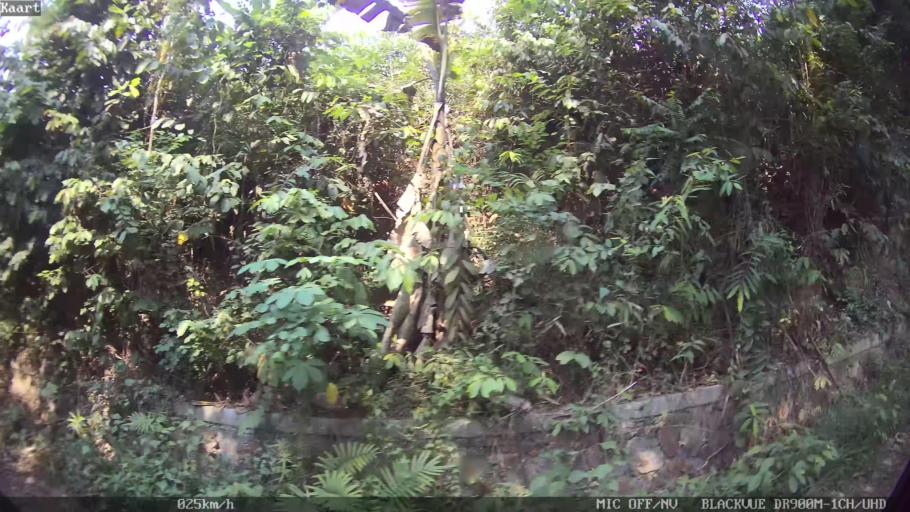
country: ID
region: Lampung
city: Pringsewu
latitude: -5.3855
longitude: 104.9934
